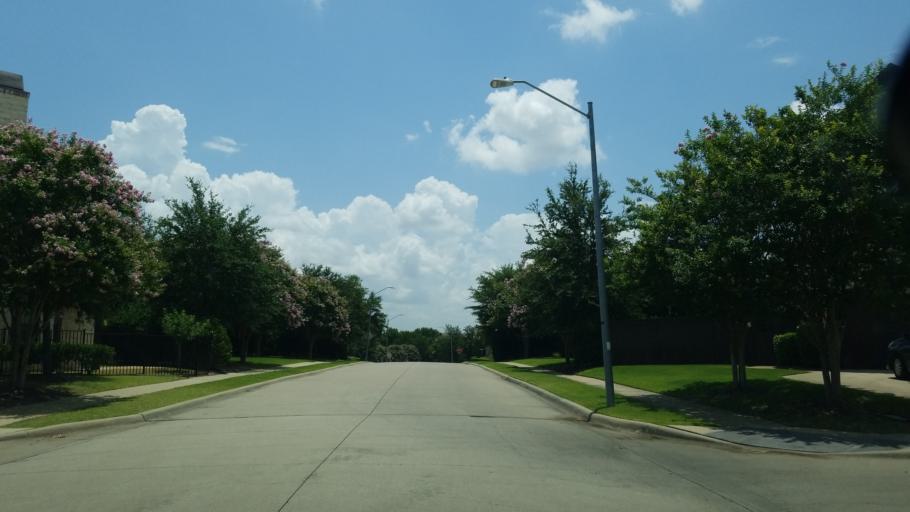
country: US
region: Texas
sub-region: Dallas County
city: Coppell
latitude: 32.9486
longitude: -96.9611
